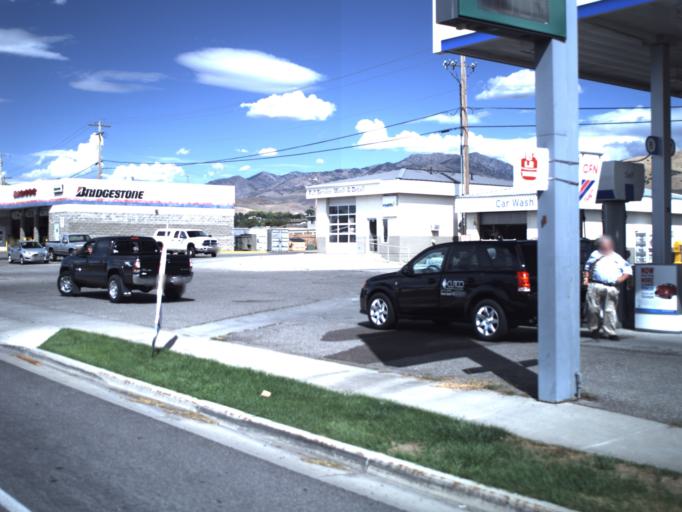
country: US
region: Utah
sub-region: Cache County
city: Smithfield
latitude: 41.8205
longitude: -111.8330
